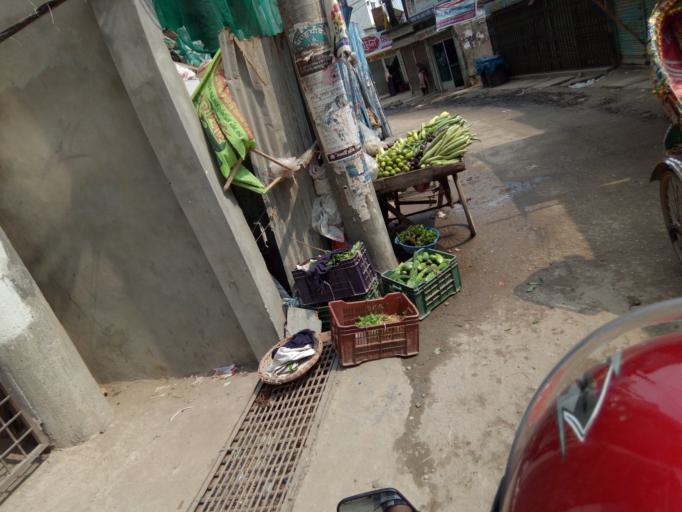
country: BD
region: Dhaka
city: Paltan
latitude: 23.7178
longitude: 90.4845
